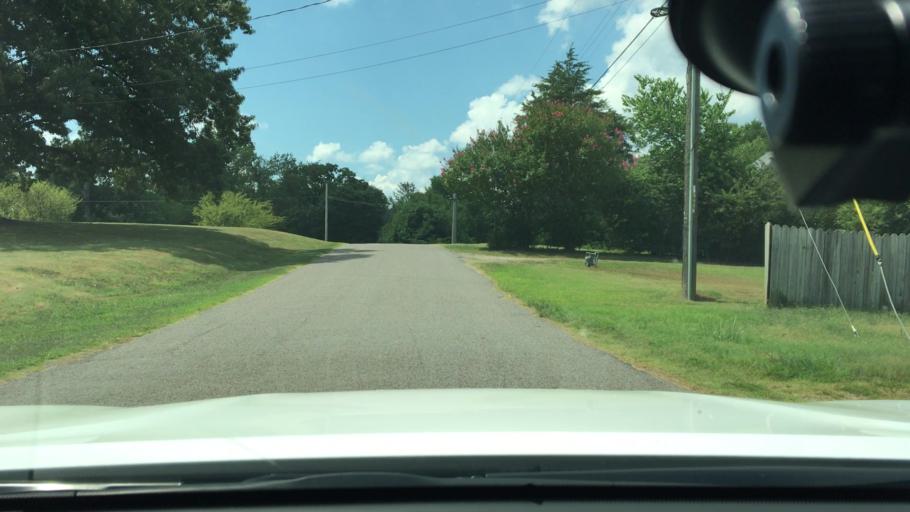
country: US
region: Arkansas
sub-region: Logan County
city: Paris
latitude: 35.2934
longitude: -93.6390
